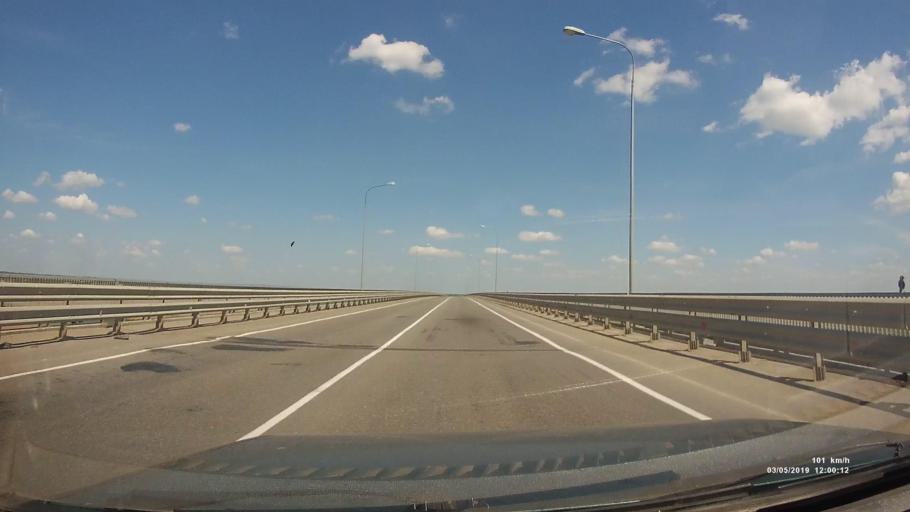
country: RU
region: Rostov
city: Bagayevskaya
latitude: 47.2458
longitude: 40.3377
